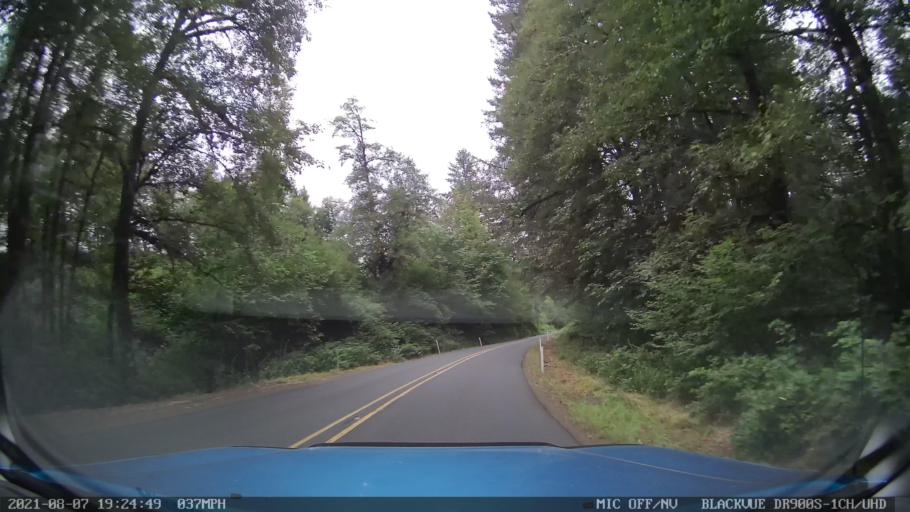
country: US
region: Oregon
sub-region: Linn County
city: Lyons
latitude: 44.8564
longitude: -122.6576
